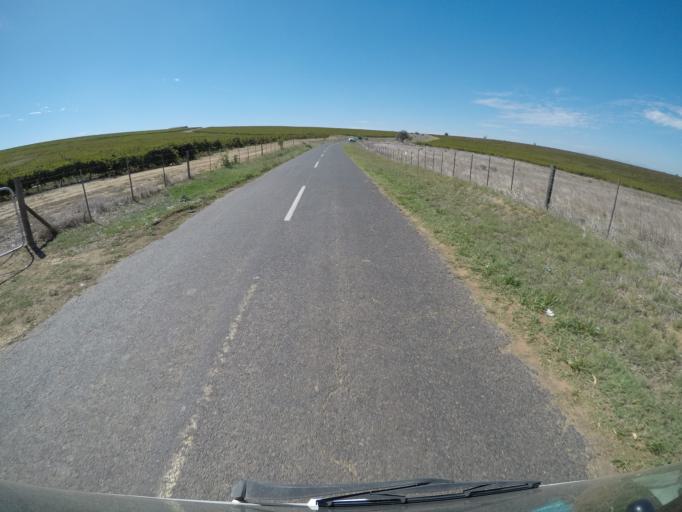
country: ZA
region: Western Cape
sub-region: City of Cape Town
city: Sunset Beach
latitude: -33.7188
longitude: 18.5773
